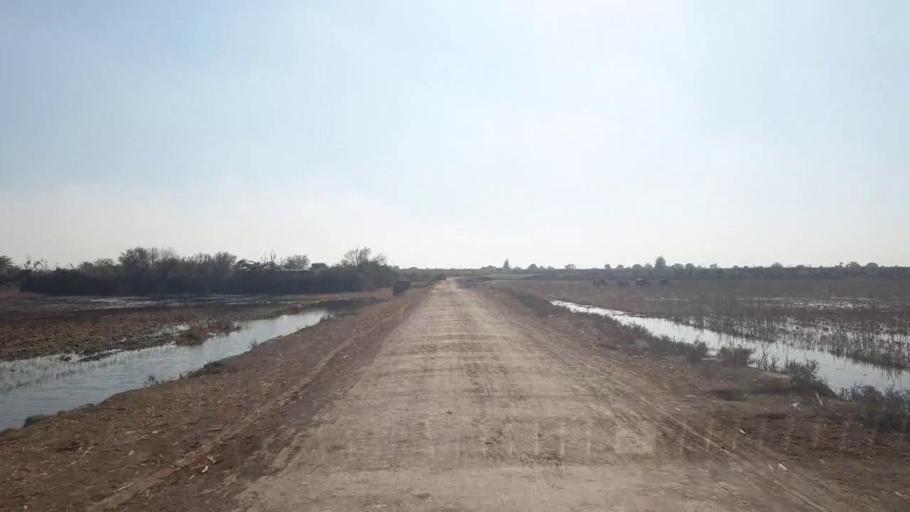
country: PK
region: Sindh
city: Shahdadpur
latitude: 25.8997
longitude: 68.5513
